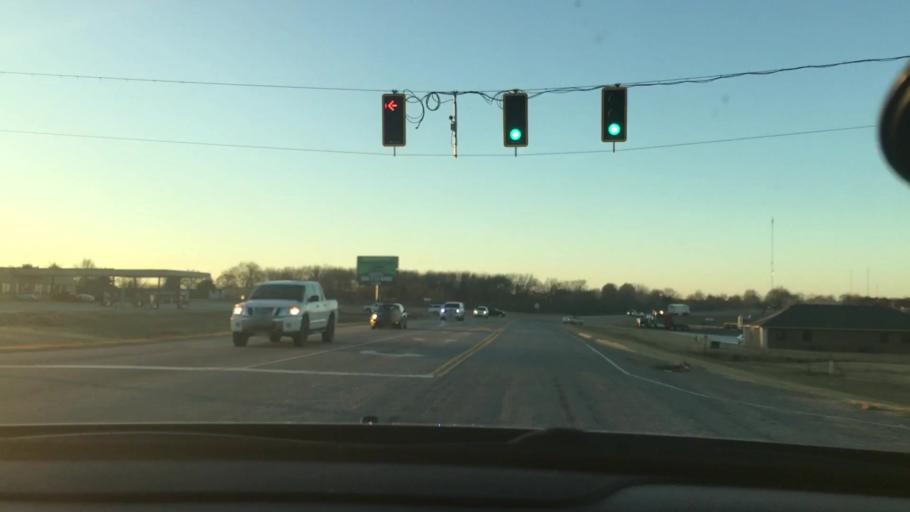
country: US
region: Oklahoma
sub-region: Pontotoc County
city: Ada
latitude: 34.7529
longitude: -96.7016
